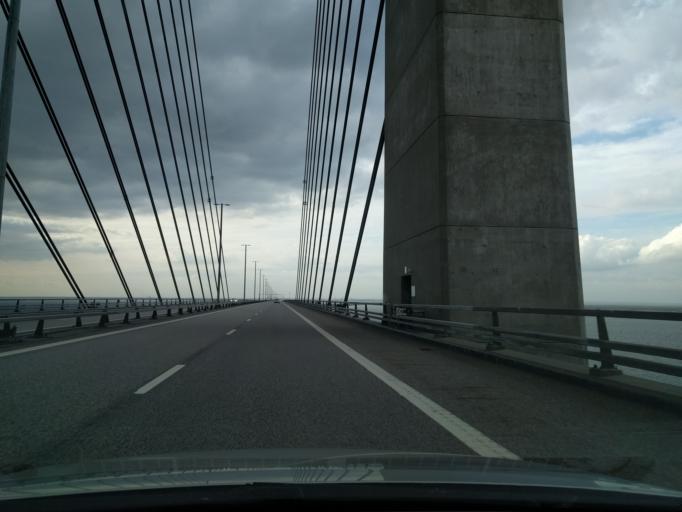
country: SE
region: Skane
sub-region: Malmo
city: Bunkeflostrand
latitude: 55.5759
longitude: 12.8222
